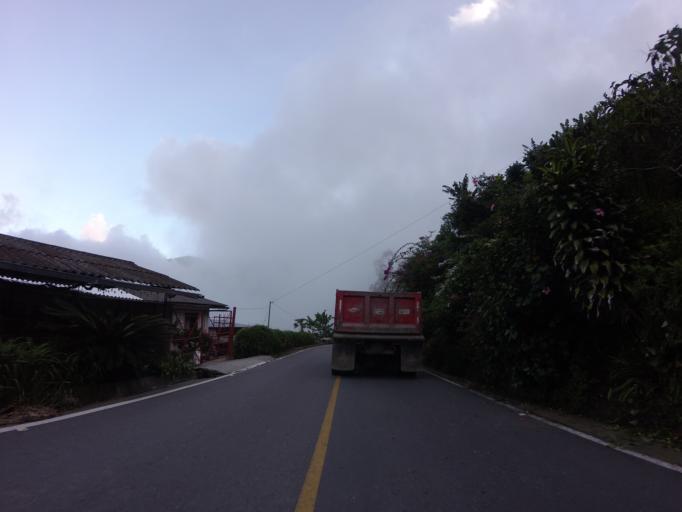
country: CO
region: Caldas
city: Manzanares
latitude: 5.3419
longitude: -75.1162
